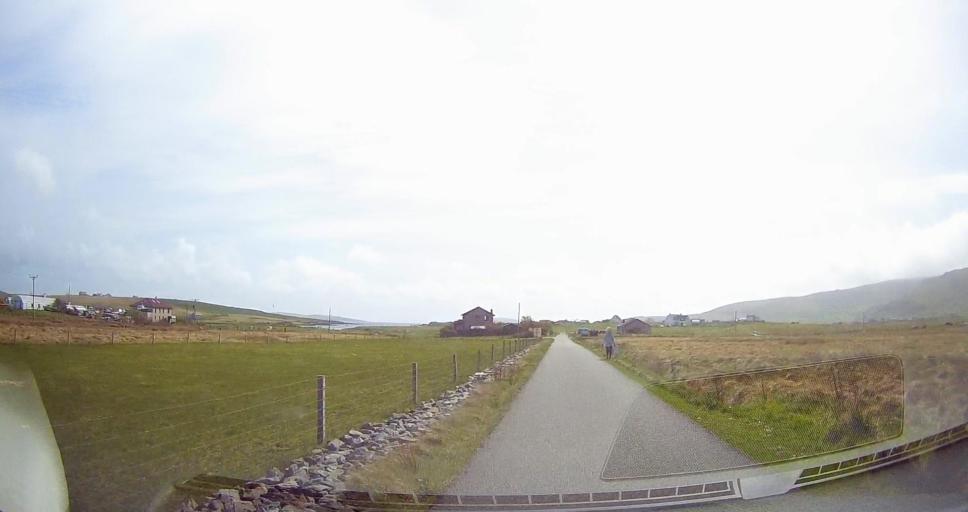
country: GB
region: Scotland
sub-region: Shetland Islands
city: Sandwick
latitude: 60.0457
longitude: -1.2166
